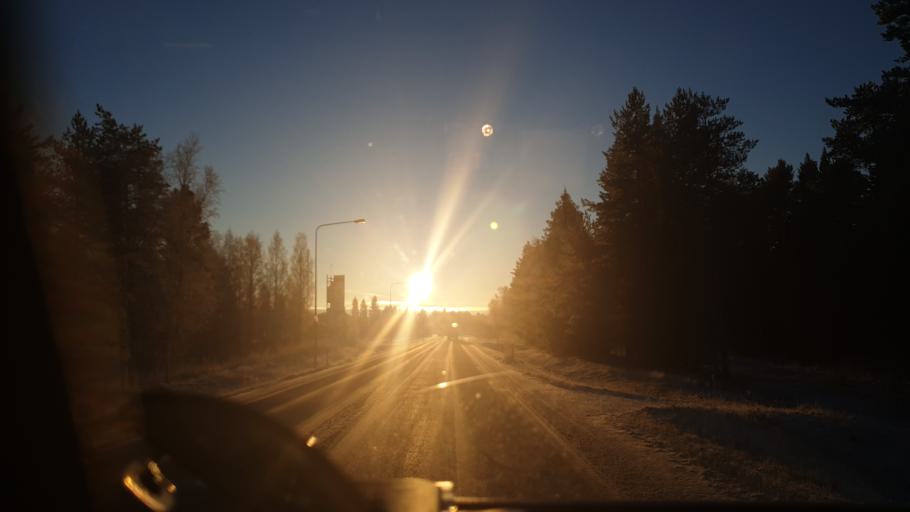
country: FI
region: Northern Ostrobothnia
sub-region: Ylivieska
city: Kalajoki
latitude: 64.2866
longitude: 23.9465
